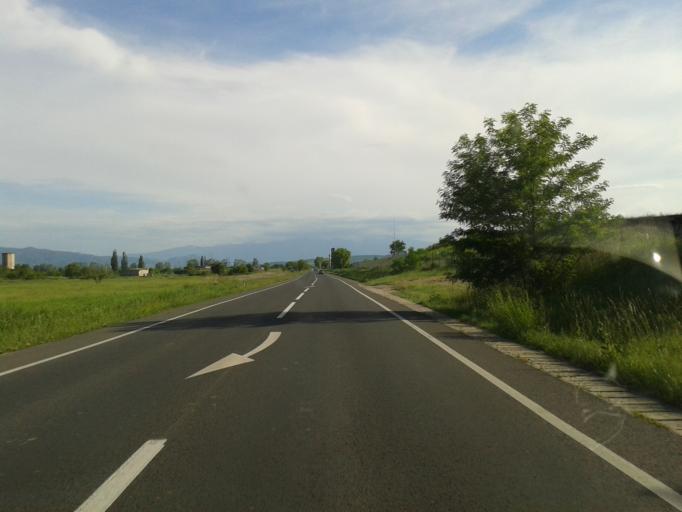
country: RO
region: Hunedoara
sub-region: Comuna Calan
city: Calan
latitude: 45.7487
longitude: 23.0007
